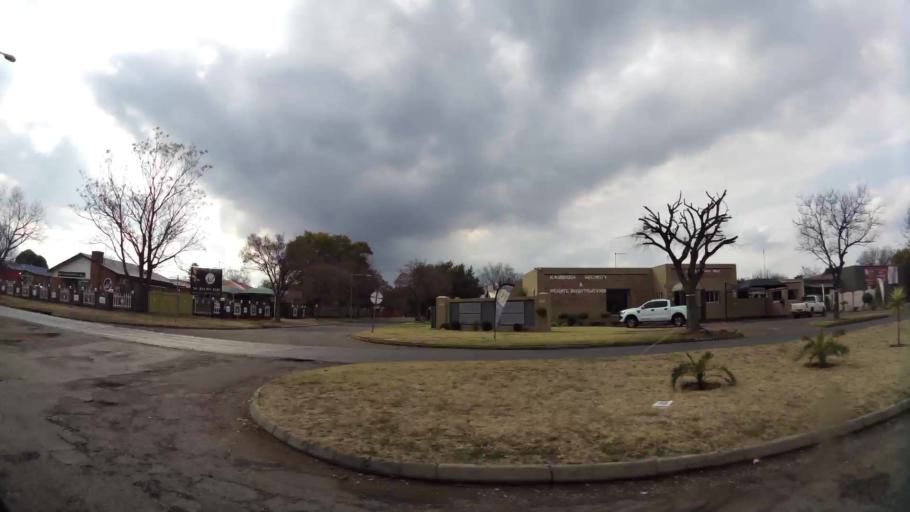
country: ZA
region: Gauteng
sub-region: Sedibeng District Municipality
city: Vanderbijlpark
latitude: -26.7220
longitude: 27.8323
